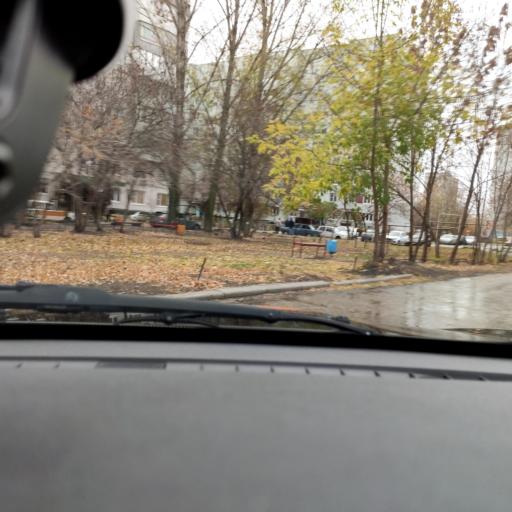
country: RU
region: Samara
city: Tol'yatti
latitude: 53.5280
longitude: 49.3092
